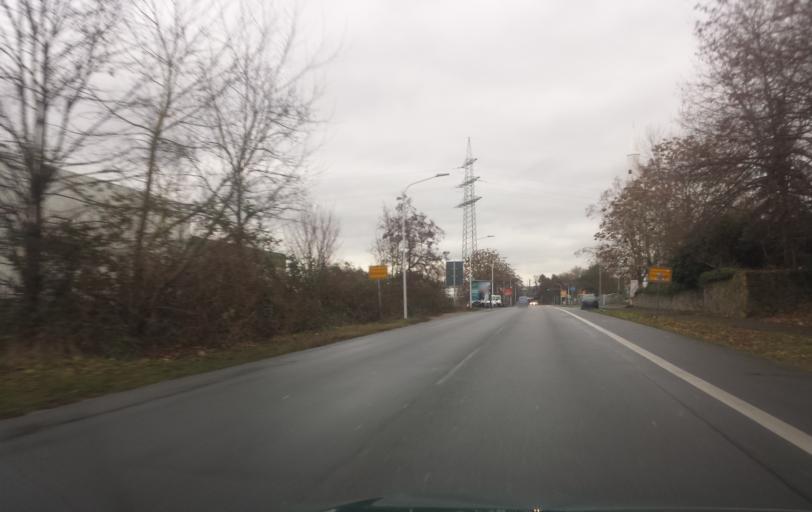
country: DE
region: Hesse
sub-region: Regierungsbezirk Darmstadt
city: Darmstadt
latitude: 49.8882
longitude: 8.6197
